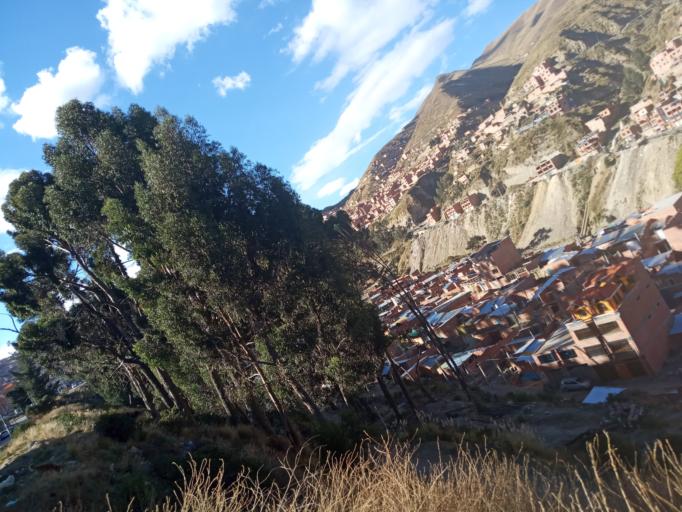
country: BO
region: La Paz
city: La Paz
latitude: -16.4557
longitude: -68.1492
